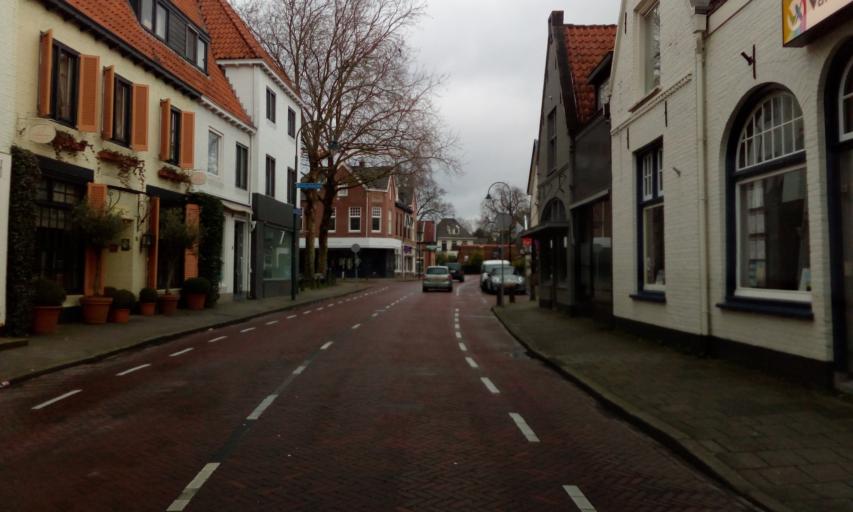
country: NL
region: North Holland
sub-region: Gemeente Laren
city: Laren
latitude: 52.2579
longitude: 5.2235
